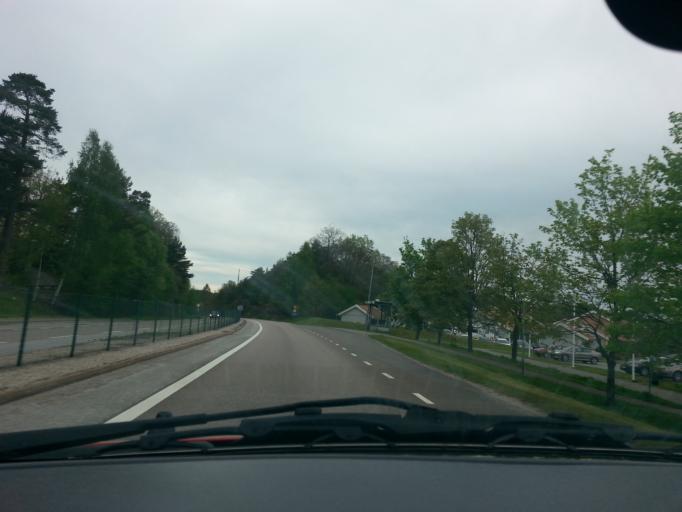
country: SE
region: Vaestra Goetaland
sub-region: Alingsas Kommun
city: Alingsas
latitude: 57.9135
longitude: 12.5556
